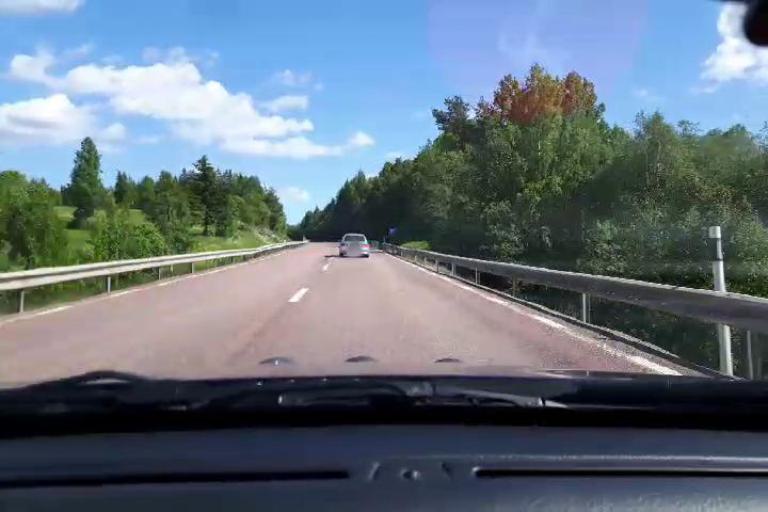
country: SE
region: Gaevleborg
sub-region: Hudiksvalls Kommun
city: Sorforsa
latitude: 61.7417
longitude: 16.8601
